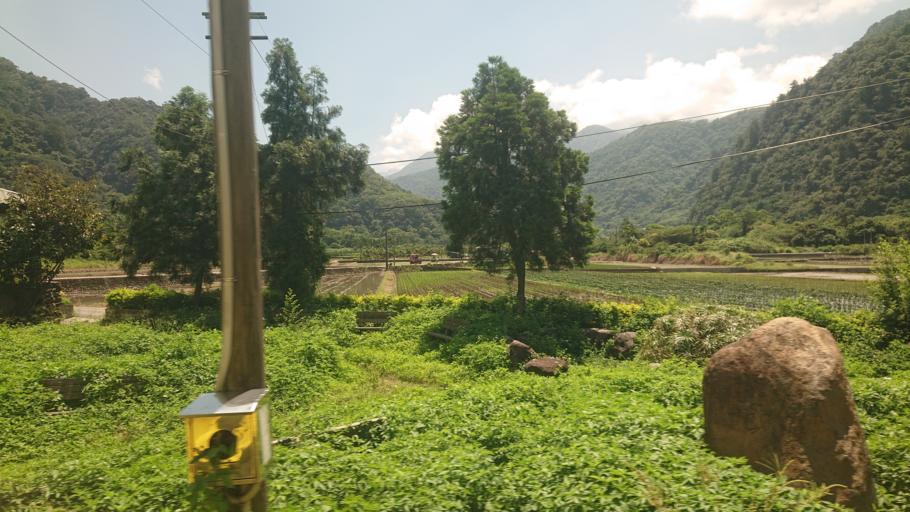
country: TW
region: Taiwan
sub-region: Nantou
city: Puli
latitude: 24.0660
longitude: 120.9531
